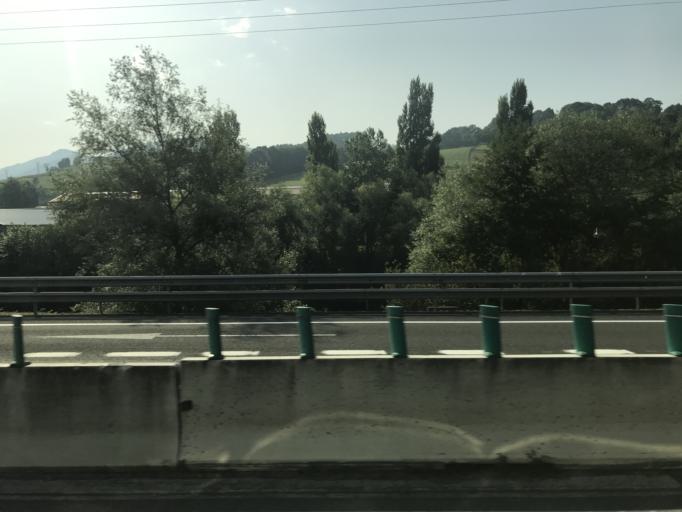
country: ES
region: Basque Country
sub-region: Provincia de Guipuzcoa
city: Andoain
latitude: 43.2082
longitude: -2.0354
